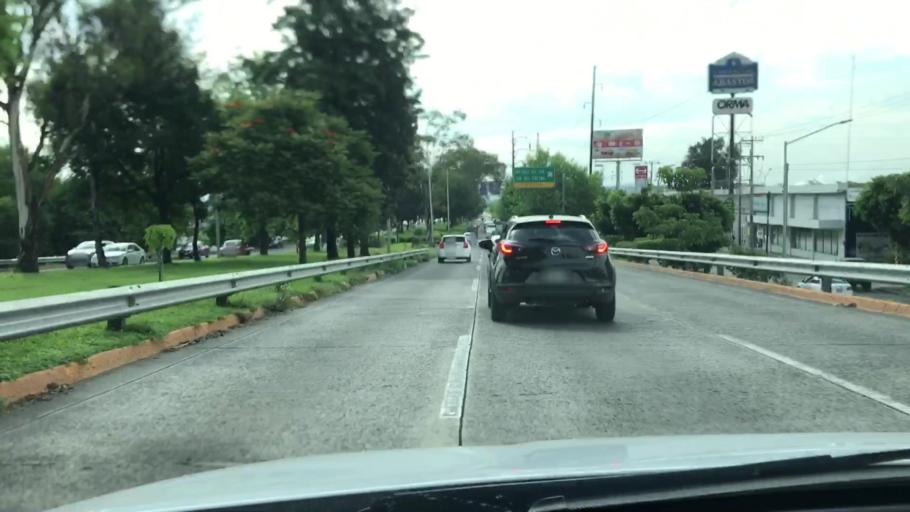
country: MX
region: Jalisco
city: Guadalajara
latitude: 20.6568
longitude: -103.3792
